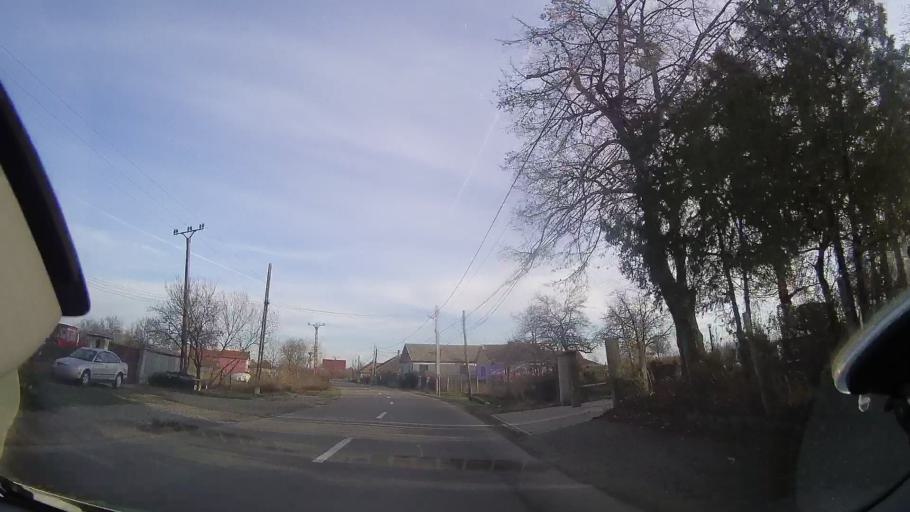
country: RO
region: Bihor
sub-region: Comuna Tileagd
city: Tileagd
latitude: 47.0688
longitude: 22.2023
